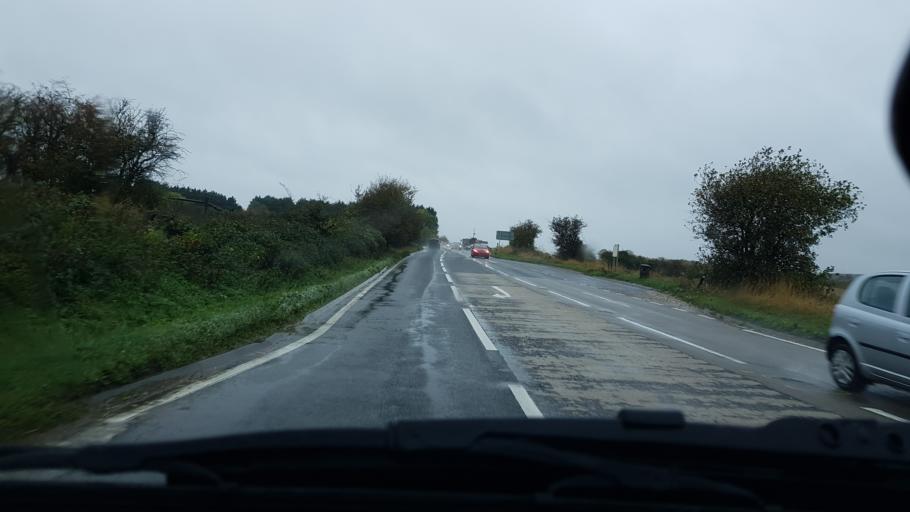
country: GB
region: England
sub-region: Oxfordshire
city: Carterton
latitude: 51.7926
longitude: -1.5979
